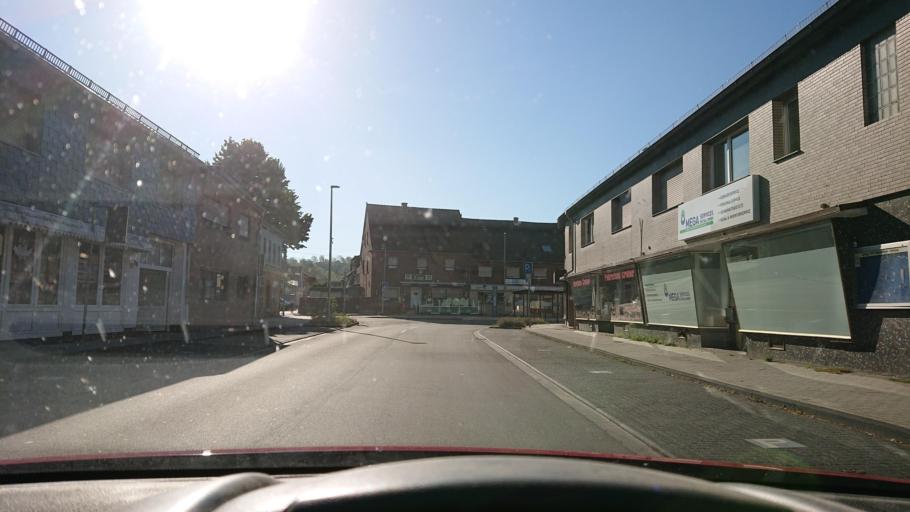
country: DE
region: North Rhine-Westphalia
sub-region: Regierungsbezirk Koln
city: Bergheim
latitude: 50.9730
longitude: 6.6784
